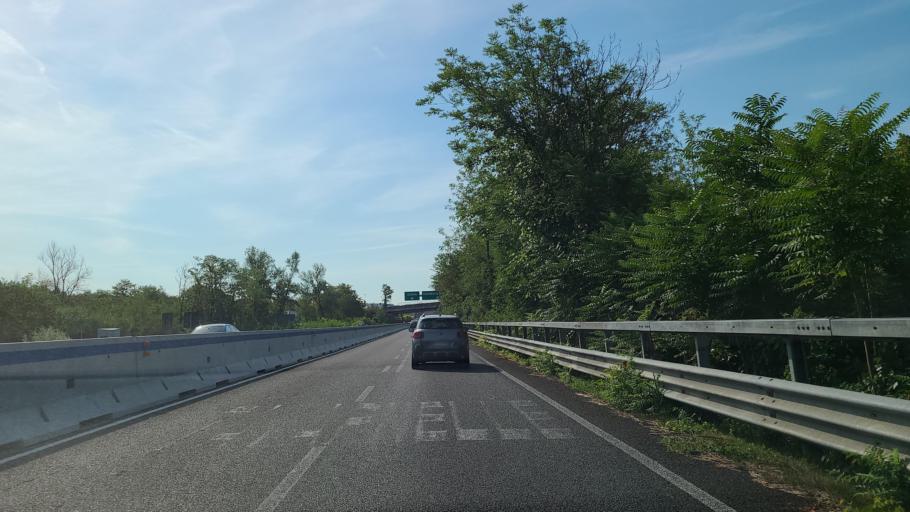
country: IT
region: Tuscany
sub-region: Province of Florence
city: Sambuca
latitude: 43.5951
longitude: 11.1968
